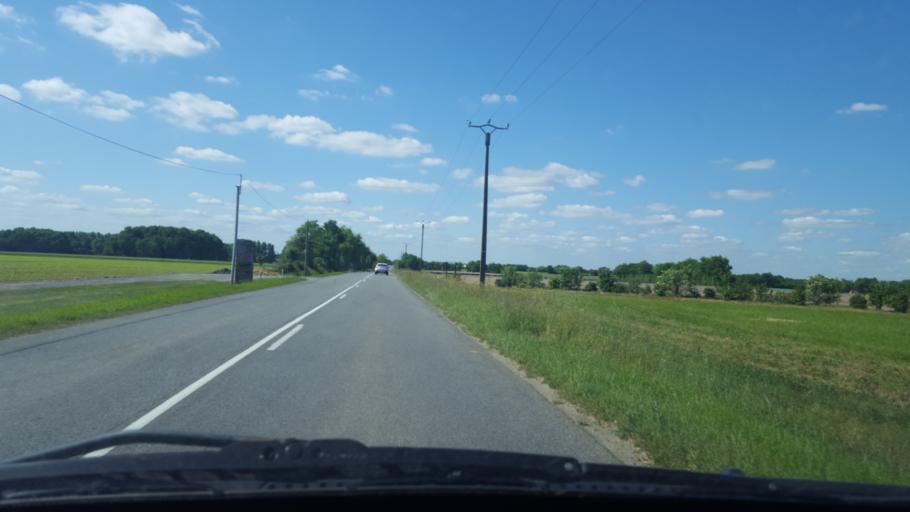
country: FR
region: Pays de la Loire
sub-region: Departement de la Loire-Atlantique
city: Geneston
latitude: 47.0402
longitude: -1.5594
